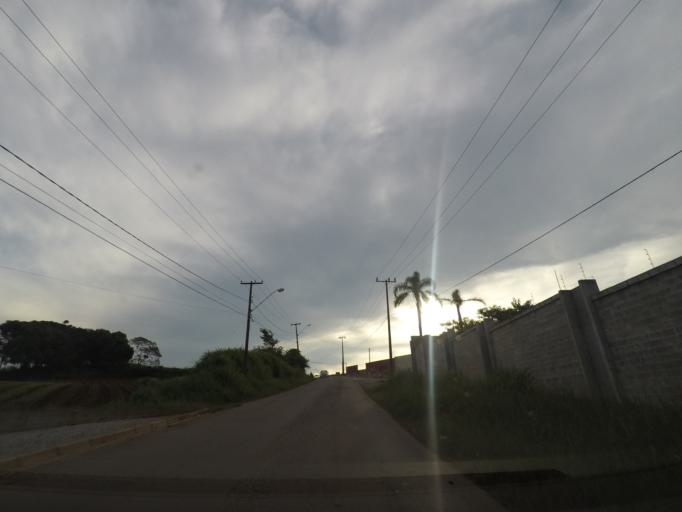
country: BR
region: Parana
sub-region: Colombo
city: Colombo
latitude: -25.2866
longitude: -49.2112
